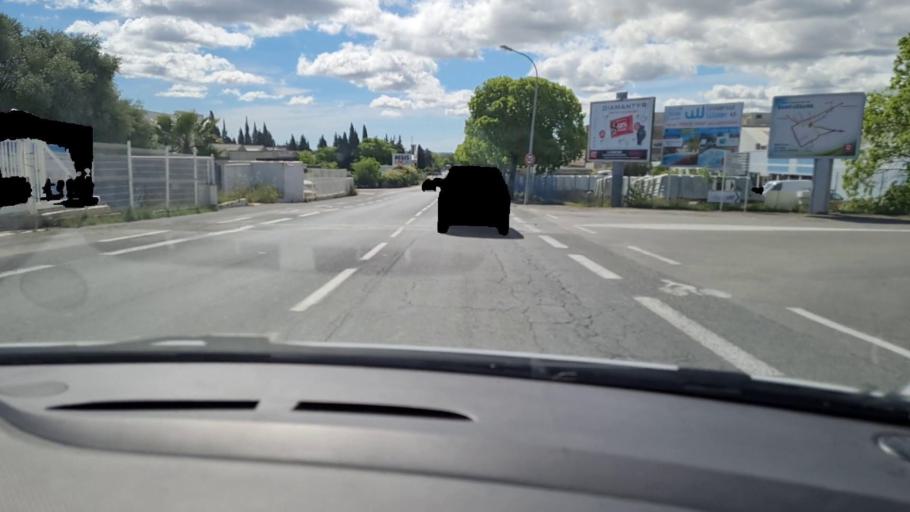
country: FR
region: Languedoc-Roussillon
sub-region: Departement du Gard
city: Milhaud
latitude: 43.8148
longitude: 4.3144
